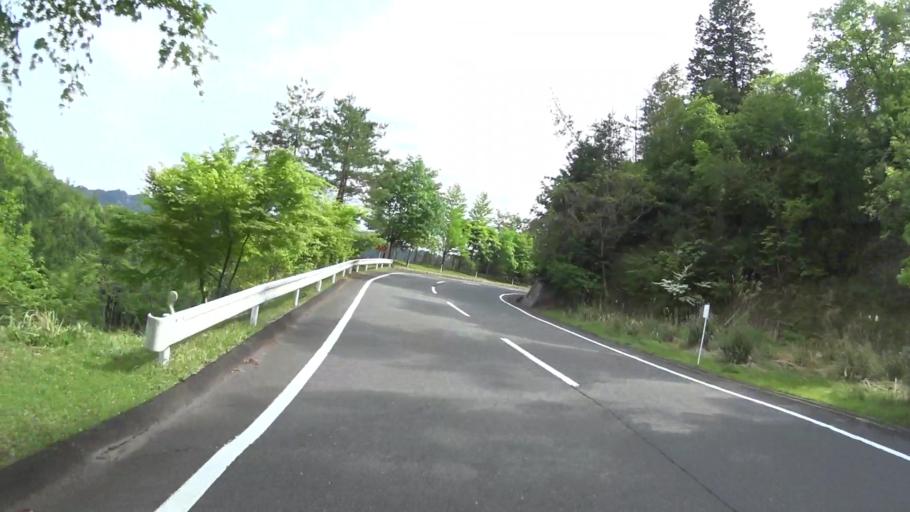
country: JP
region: Kyoto
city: Kameoka
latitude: 35.1490
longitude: 135.6247
